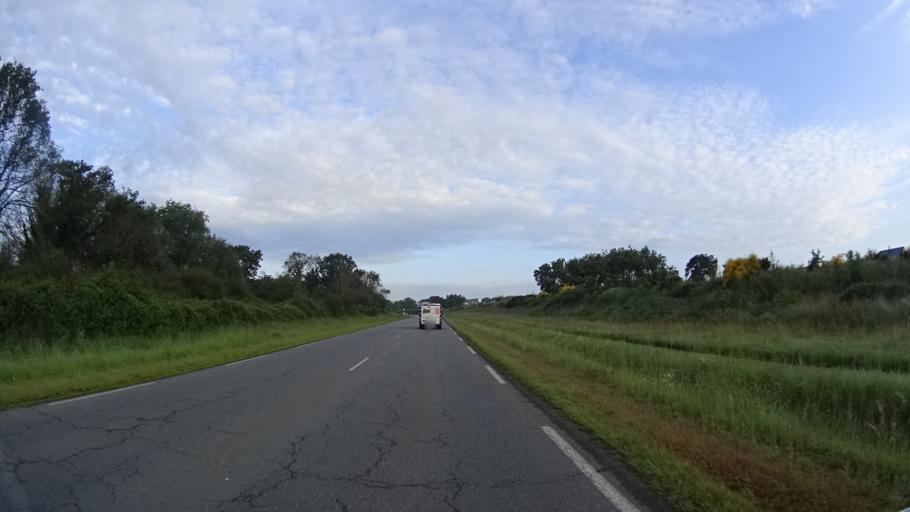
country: FR
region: Brittany
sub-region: Departement du Morbihan
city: Sene
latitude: 47.6430
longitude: -2.7370
